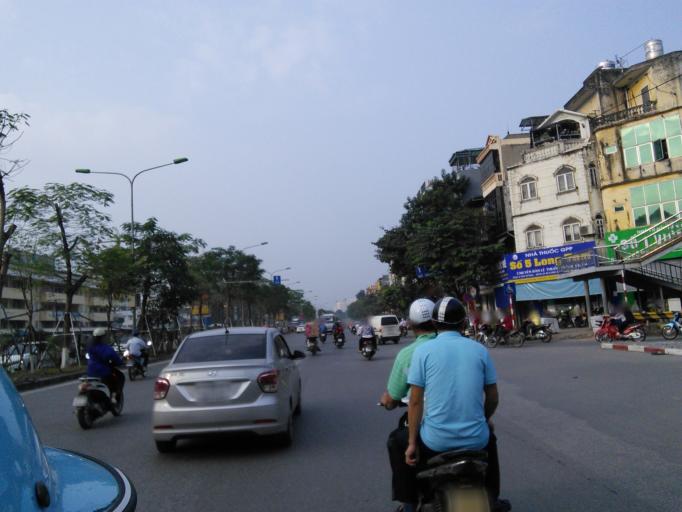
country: VN
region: Ha Noi
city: Hai BaTrung
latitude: 21.0019
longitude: 105.8414
